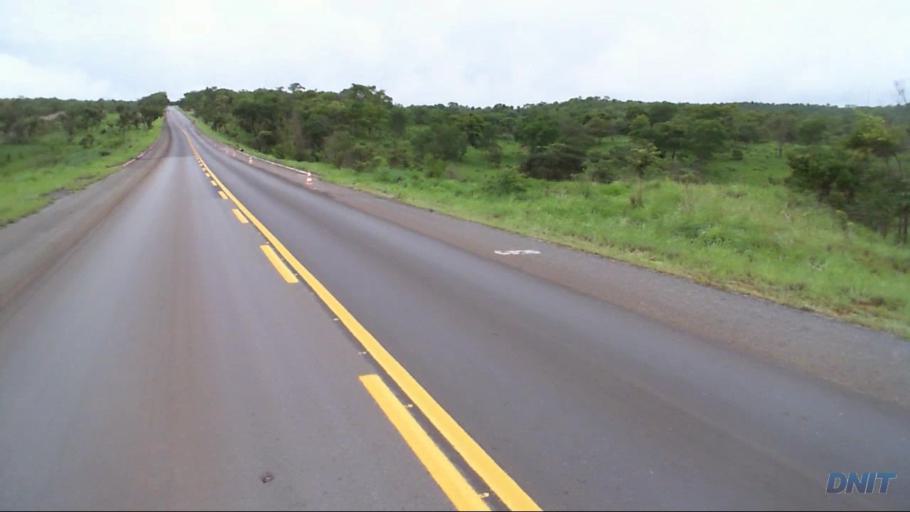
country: BR
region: Goias
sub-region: Padre Bernardo
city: Padre Bernardo
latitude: -15.1864
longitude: -48.4326
